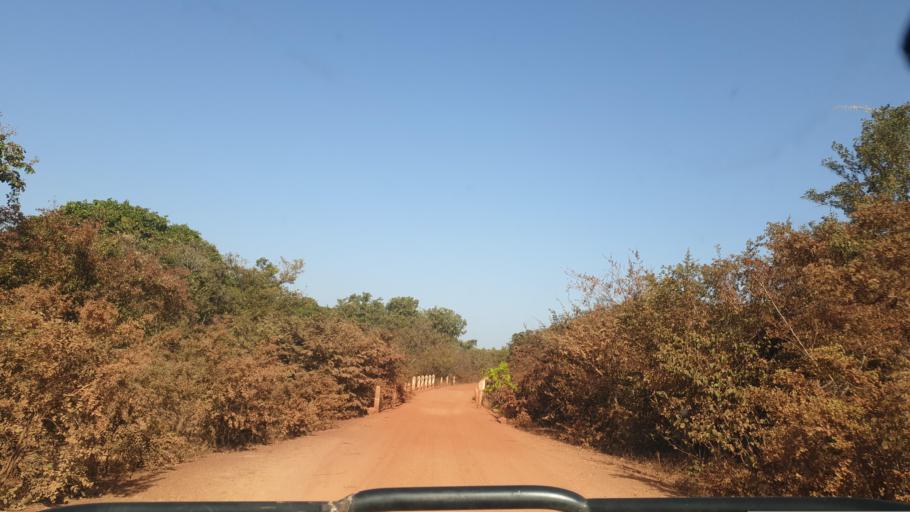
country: ML
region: Sikasso
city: Bougouni
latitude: 11.7779
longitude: -6.9072
